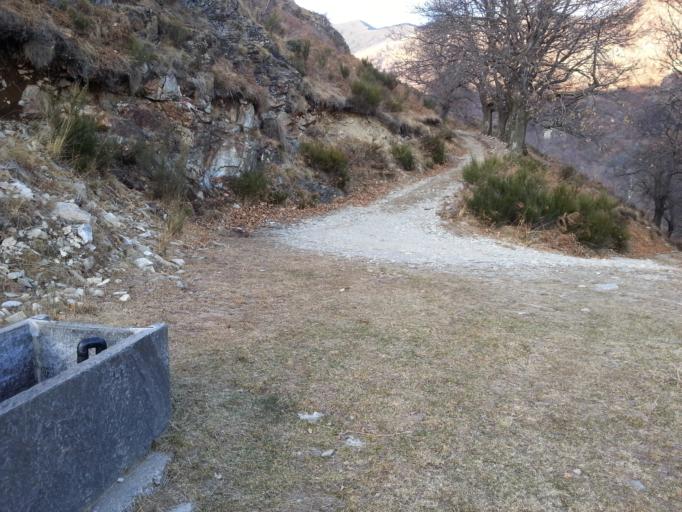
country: CH
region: Ticino
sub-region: Lugano District
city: Gravesano
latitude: 46.0550
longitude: 8.8805
